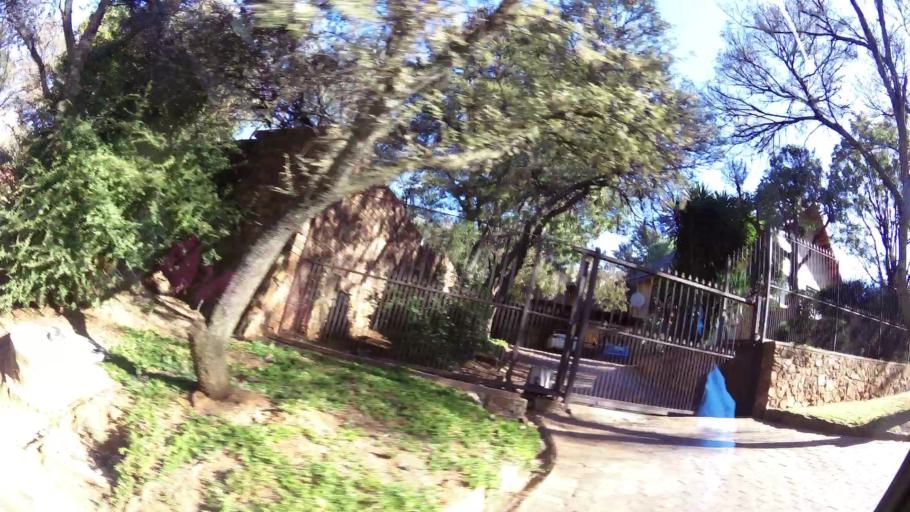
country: ZA
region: Gauteng
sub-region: City of Johannesburg Metropolitan Municipality
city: Johannesburg
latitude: -26.2810
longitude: 28.0513
